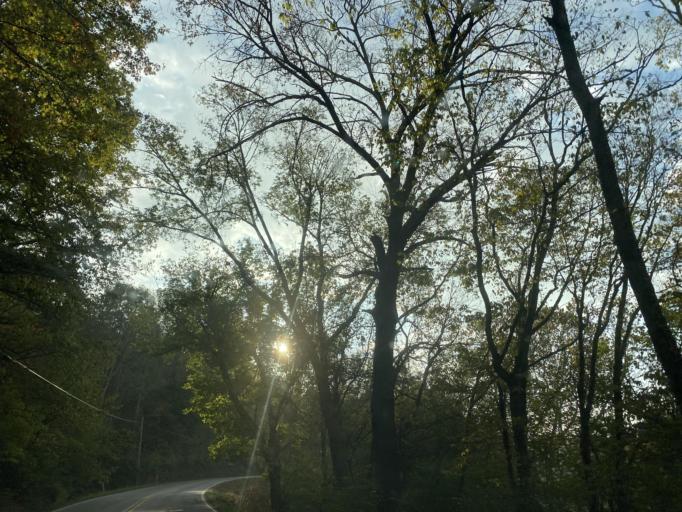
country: US
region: Kentucky
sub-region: Pendleton County
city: Falmouth
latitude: 38.7898
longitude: -84.3402
